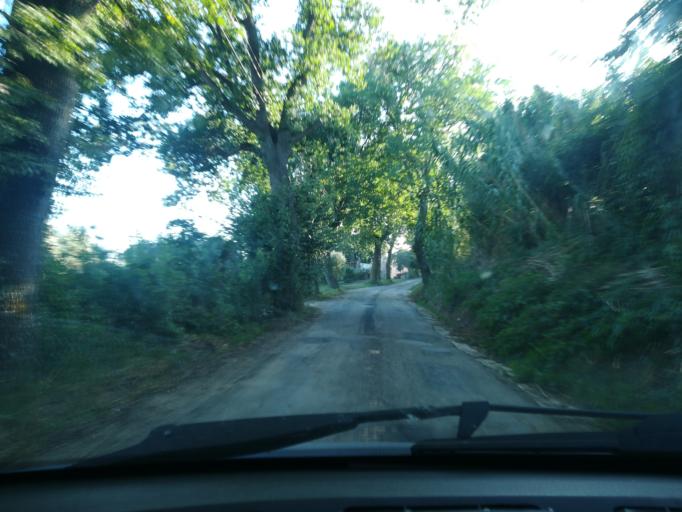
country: IT
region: The Marches
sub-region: Provincia di Macerata
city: Macerata
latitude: 43.2794
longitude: 13.4516
